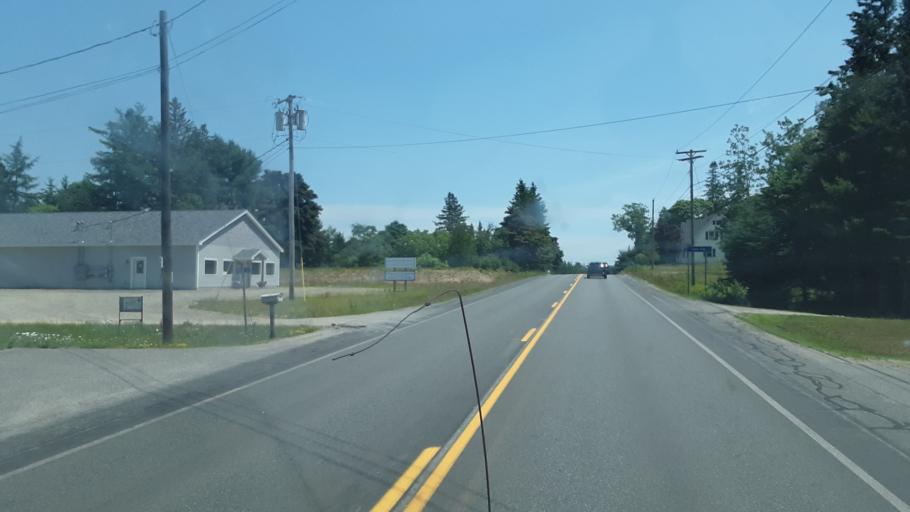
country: US
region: Maine
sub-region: Hancock County
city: Hancock
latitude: 44.5251
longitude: -68.2428
